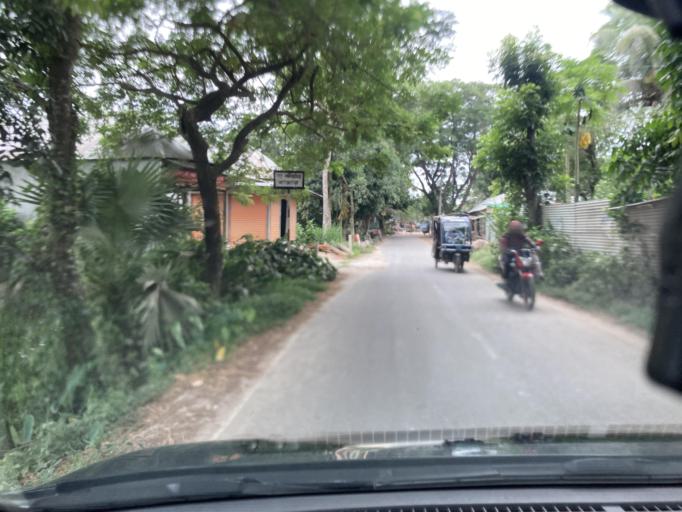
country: BD
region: Dhaka
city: Dohar
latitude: 23.7829
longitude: 90.0660
